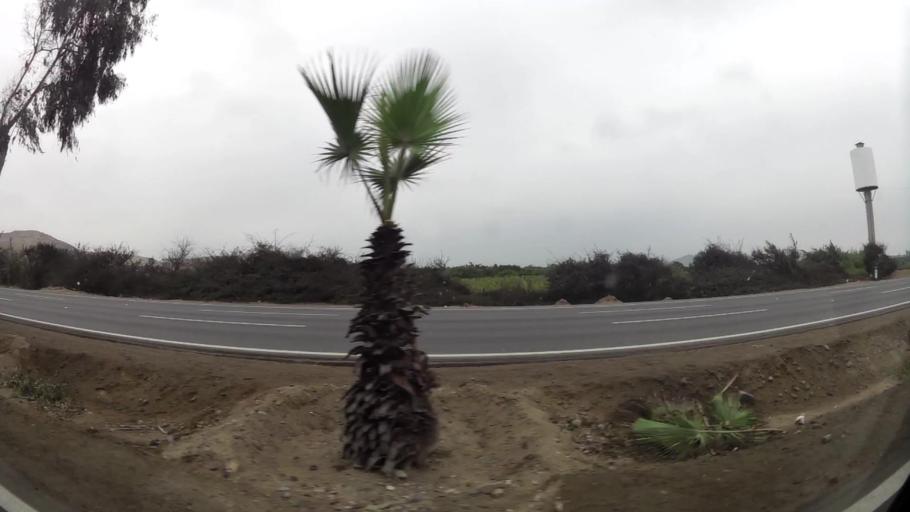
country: PE
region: Lima
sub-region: Lima
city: Punta Hermosa
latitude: -12.2709
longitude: -76.8981
